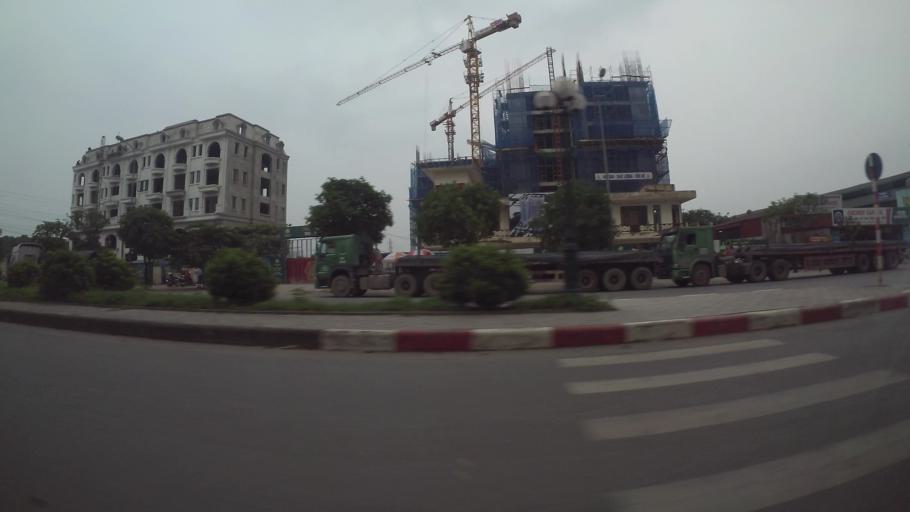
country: VN
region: Ha Noi
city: Trau Quy
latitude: 21.0396
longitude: 105.9127
